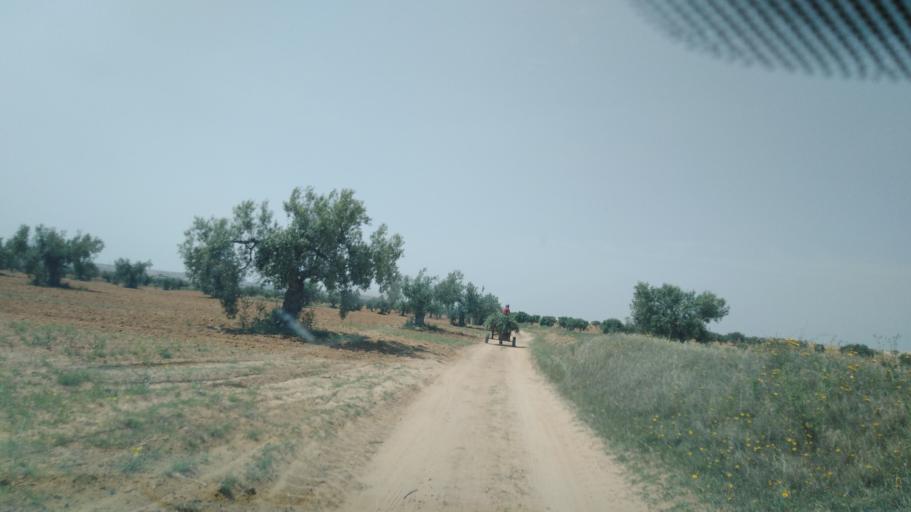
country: TN
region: Safaqis
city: Sfax
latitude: 34.7635
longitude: 10.5794
